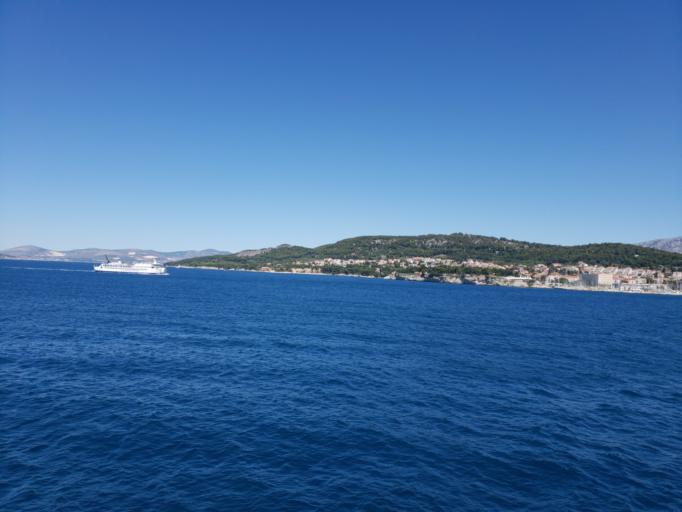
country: HR
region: Splitsko-Dalmatinska
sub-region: Grad Split
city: Split
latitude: 43.4936
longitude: 16.4336
